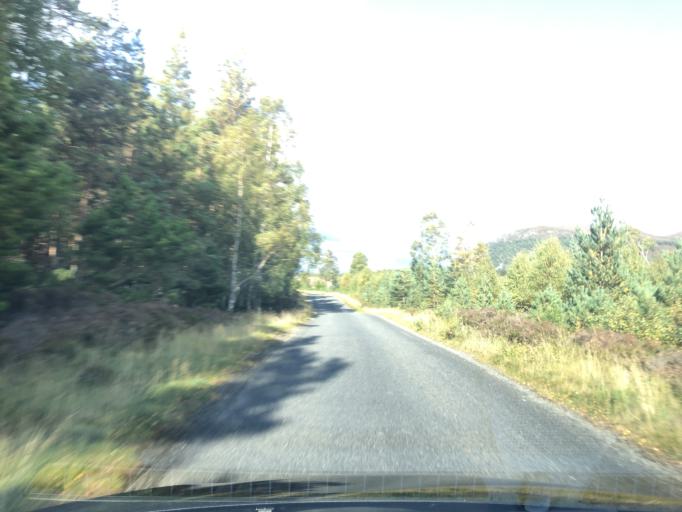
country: GB
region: Scotland
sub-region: Highland
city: Aviemore
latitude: 57.0746
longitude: -3.9014
